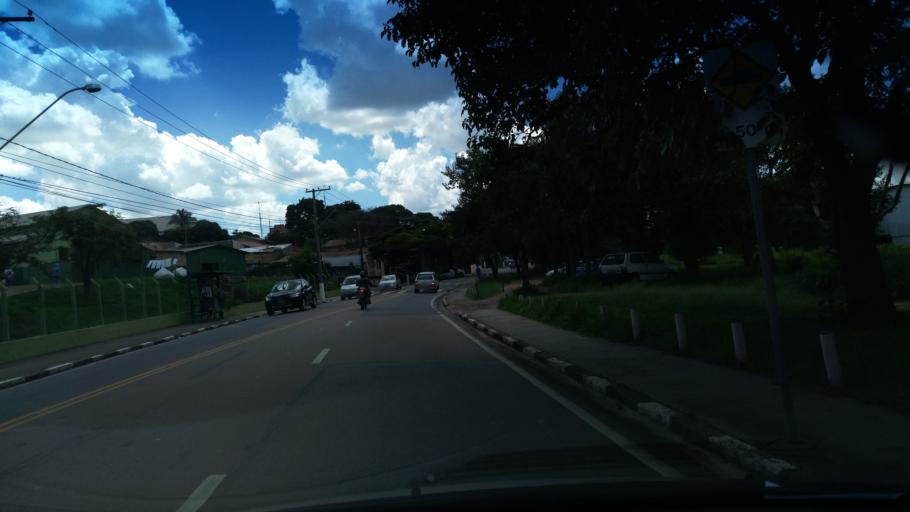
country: BR
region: Sao Paulo
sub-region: Vinhedo
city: Vinhedo
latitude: -23.0224
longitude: -46.9821
